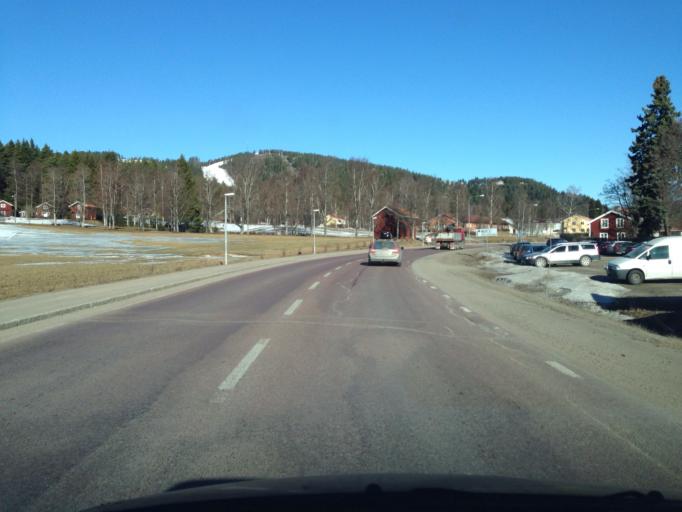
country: SE
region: Gaevleborg
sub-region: Ljusdals Kommun
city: Jaervsoe
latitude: 61.7057
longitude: 16.1635
